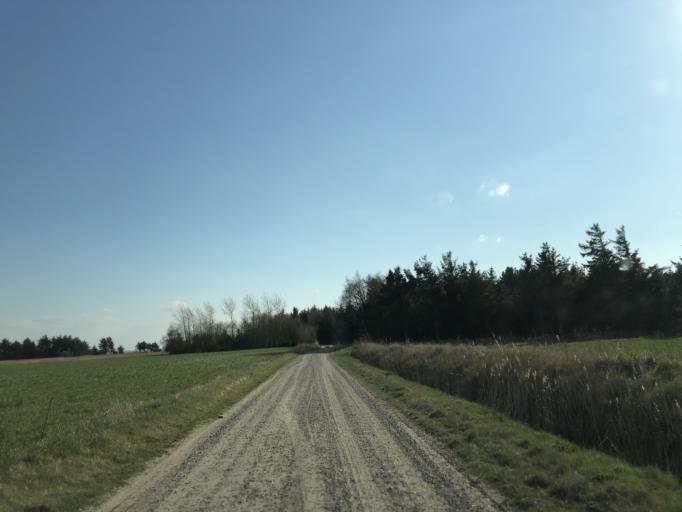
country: DK
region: Central Jutland
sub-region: Holstebro Kommune
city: Ulfborg
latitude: 56.3534
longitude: 8.2477
